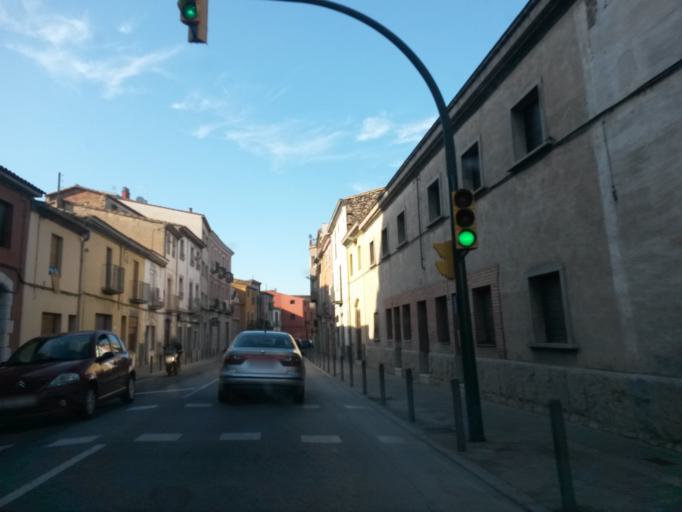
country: ES
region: Catalonia
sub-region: Provincia de Girona
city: Sarria de Ter
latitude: 42.0111
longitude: 2.8253
